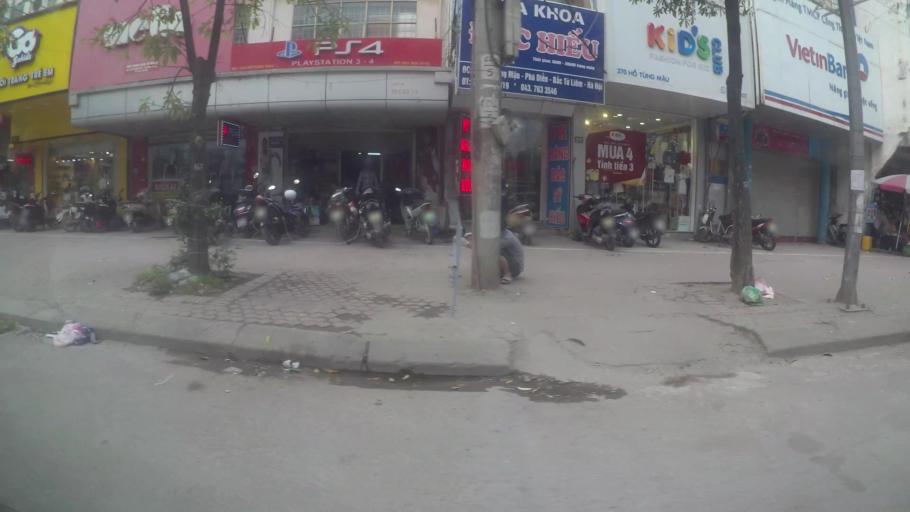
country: VN
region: Ha Noi
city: Cau Dien
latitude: 21.0412
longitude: 105.7636
